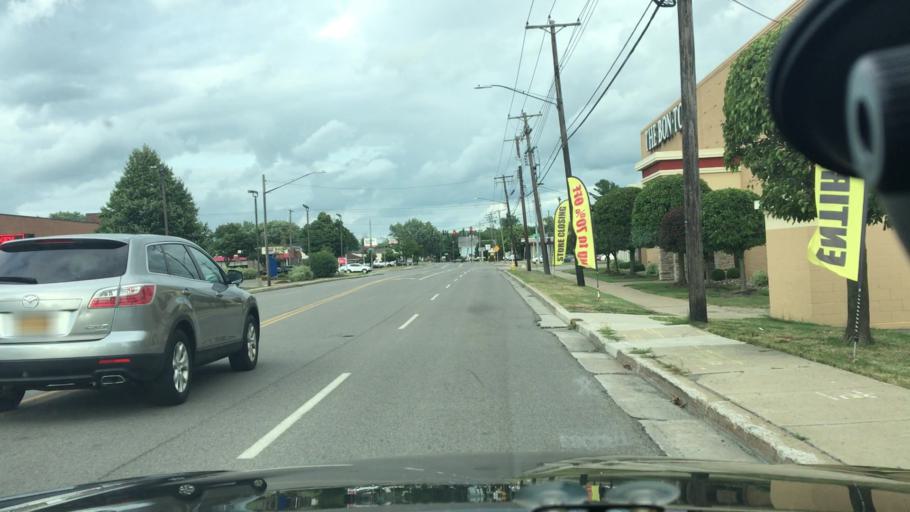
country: US
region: New York
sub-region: Erie County
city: West Seneca
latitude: 42.8301
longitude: -78.7553
